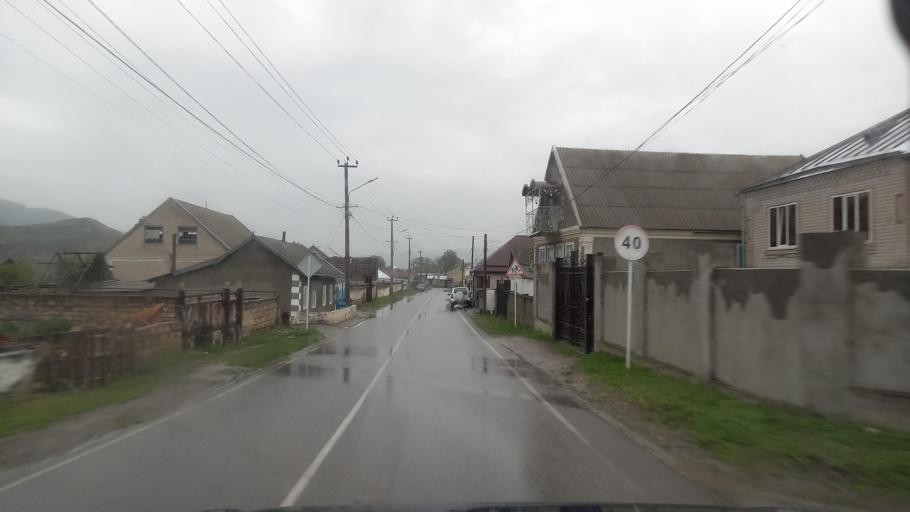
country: RU
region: Kabardino-Balkariya
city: Gundelen
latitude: 43.5955
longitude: 43.1675
